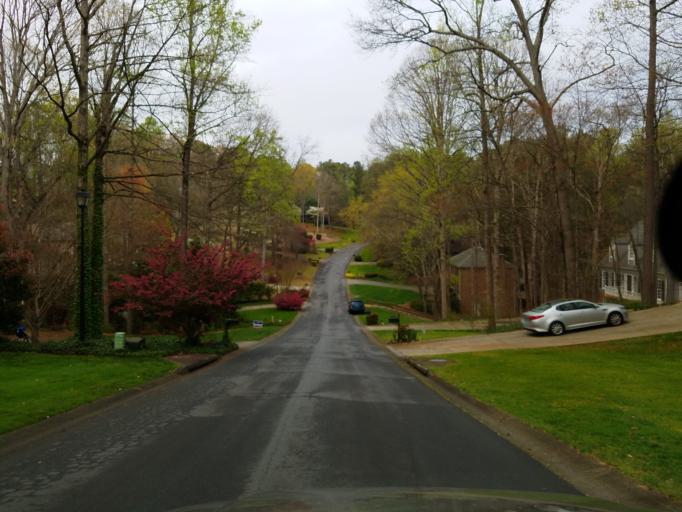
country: US
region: Georgia
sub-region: Fulton County
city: Roswell
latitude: 34.0348
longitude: -84.4229
